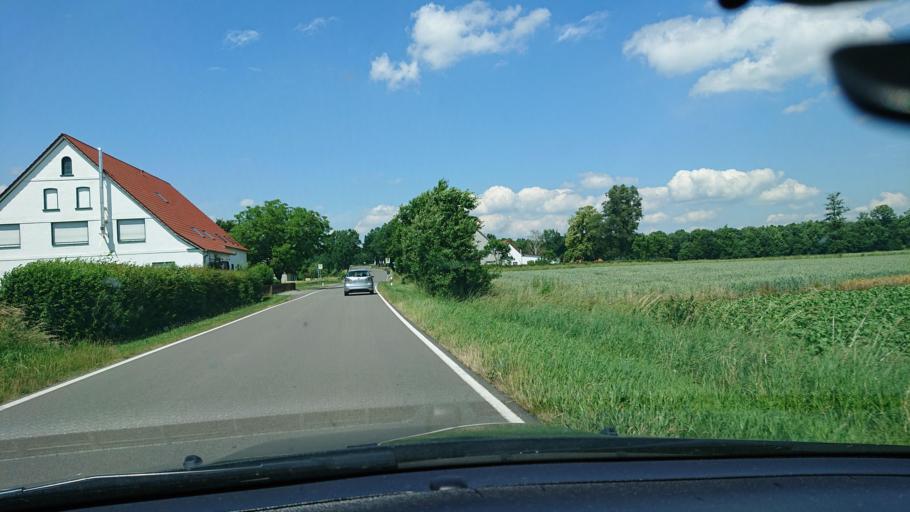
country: DE
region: North Rhine-Westphalia
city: Preussisch Oldendorf
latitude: 52.3379
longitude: 8.4610
